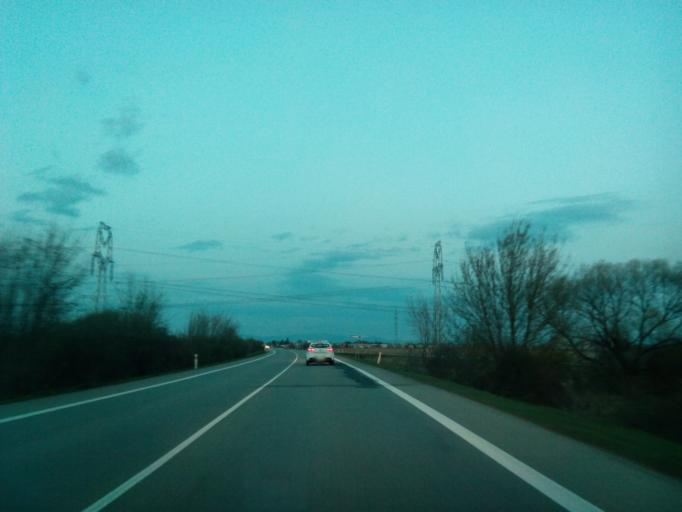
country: SK
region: Kosicky
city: Moldava nad Bodvou
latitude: 48.5980
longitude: 21.0419
